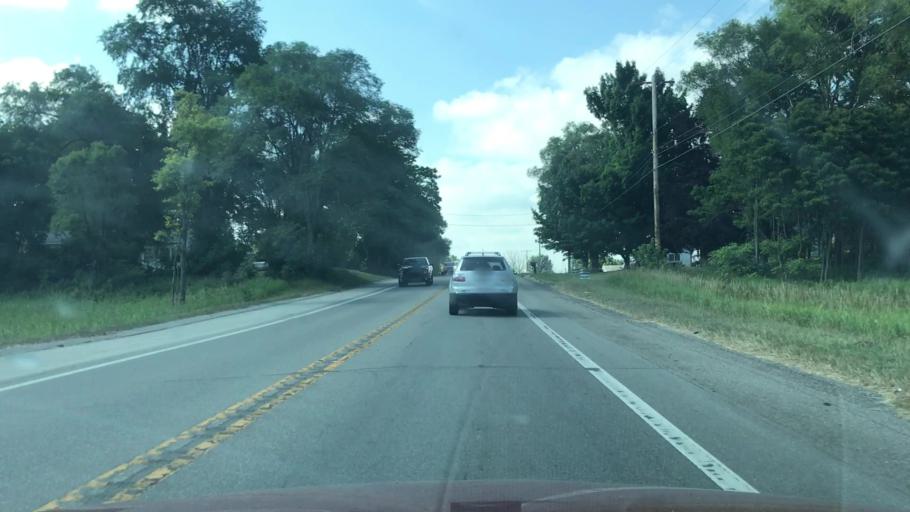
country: US
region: Michigan
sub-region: Newaygo County
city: Newaygo
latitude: 43.3120
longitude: -85.8106
